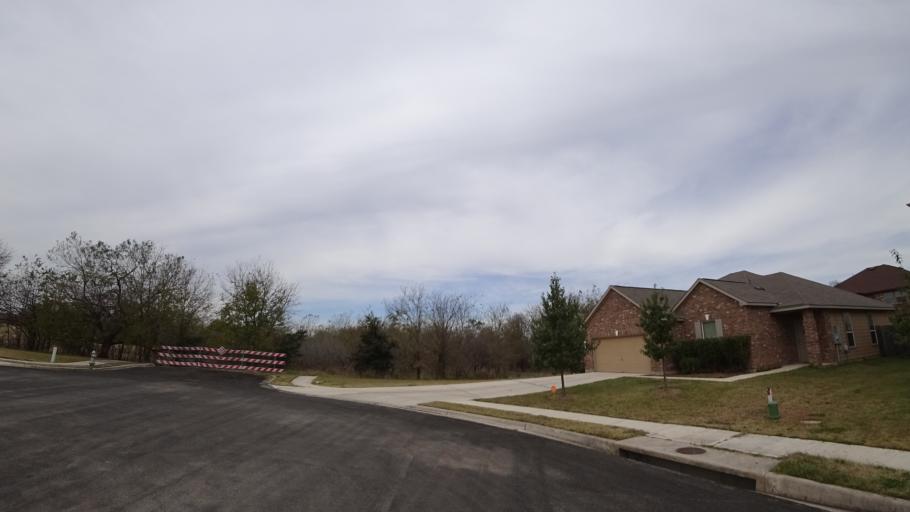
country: US
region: Texas
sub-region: Travis County
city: Onion Creek
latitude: 30.1553
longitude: -97.7449
